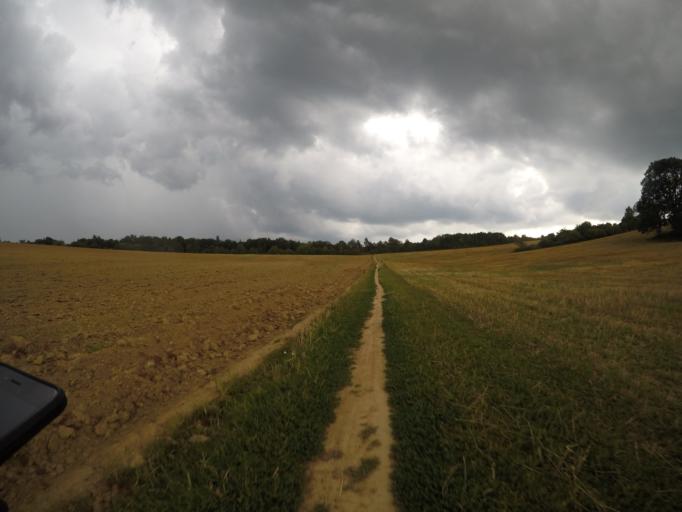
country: SK
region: Trenciansky
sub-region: Okres Trencin
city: Trencin
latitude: 48.8730
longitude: 18.0729
